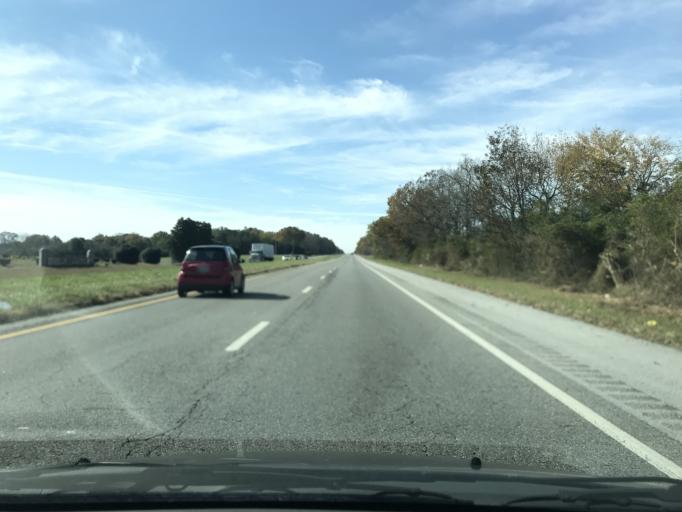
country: US
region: Tennessee
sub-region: Coffee County
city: Tullahoma
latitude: 35.3975
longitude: -86.1402
